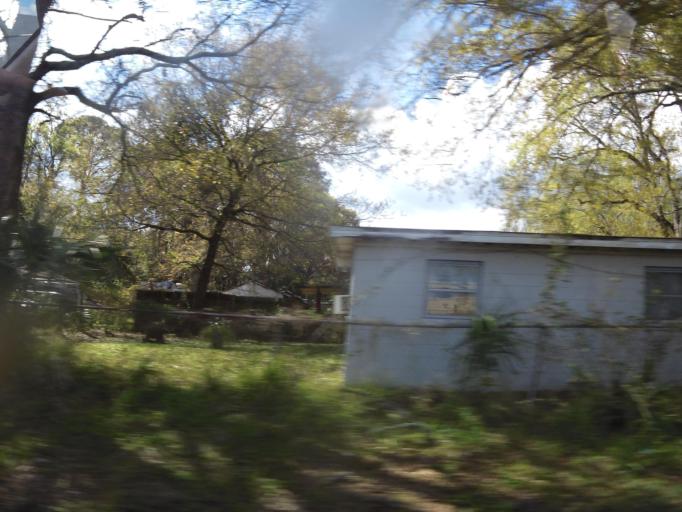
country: US
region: Florida
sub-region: Duval County
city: Jacksonville
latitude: 30.3427
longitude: -81.7141
